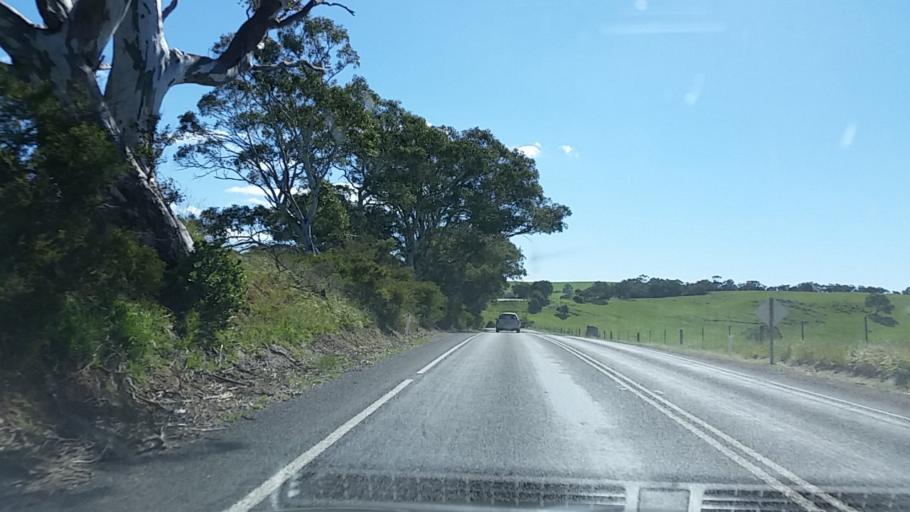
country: AU
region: South Australia
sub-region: Alexandrina
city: Strathalbyn
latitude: -35.2298
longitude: 138.8530
